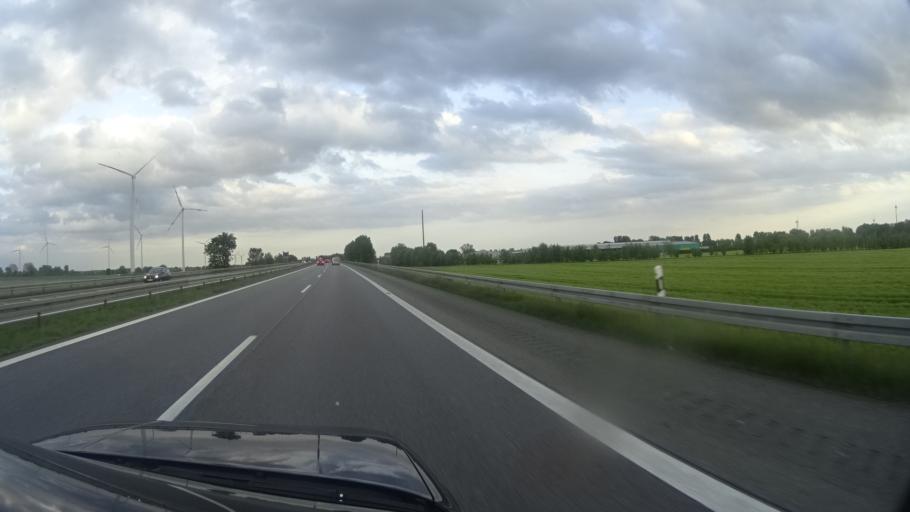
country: DE
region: Brandenburg
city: Dabergotz
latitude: 52.9175
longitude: 12.7204
